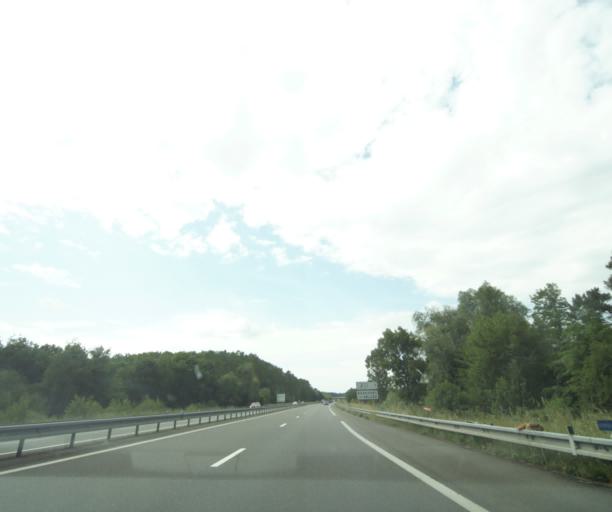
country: FR
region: Pays de la Loire
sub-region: Departement de Maine-et-Loire
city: Brion
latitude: 47.4219
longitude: -0.1387
